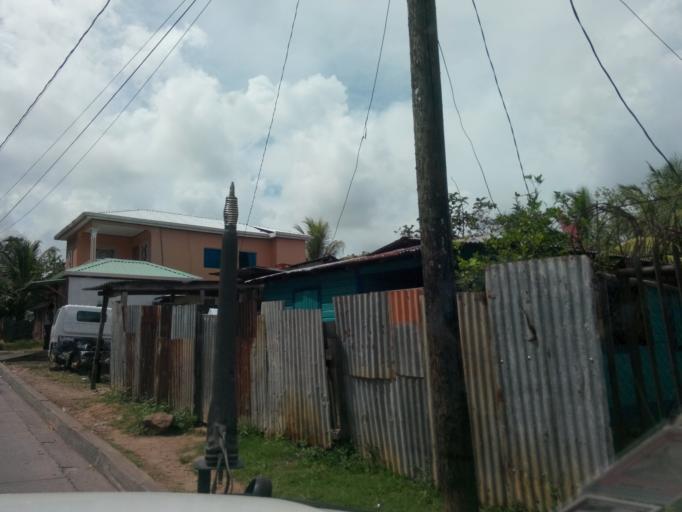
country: NI
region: Atlantico Sur
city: Bluefields
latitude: 12.0093
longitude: -83.7653
